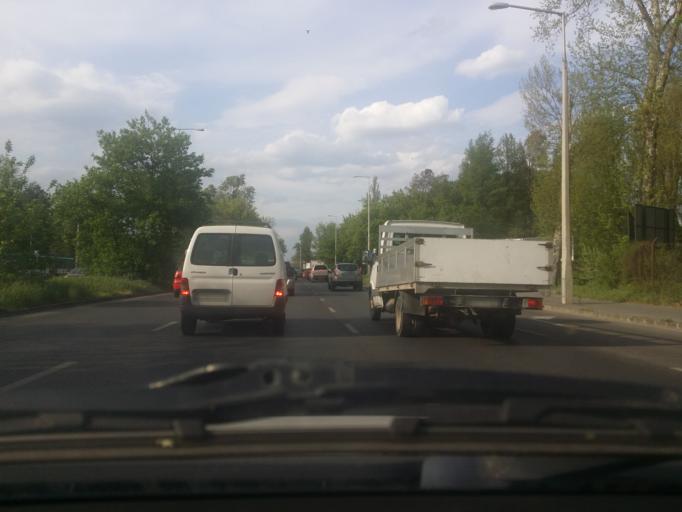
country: HU
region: Budapest
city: Budapest III. keruelet
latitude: 47.5746
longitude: 19.0488
